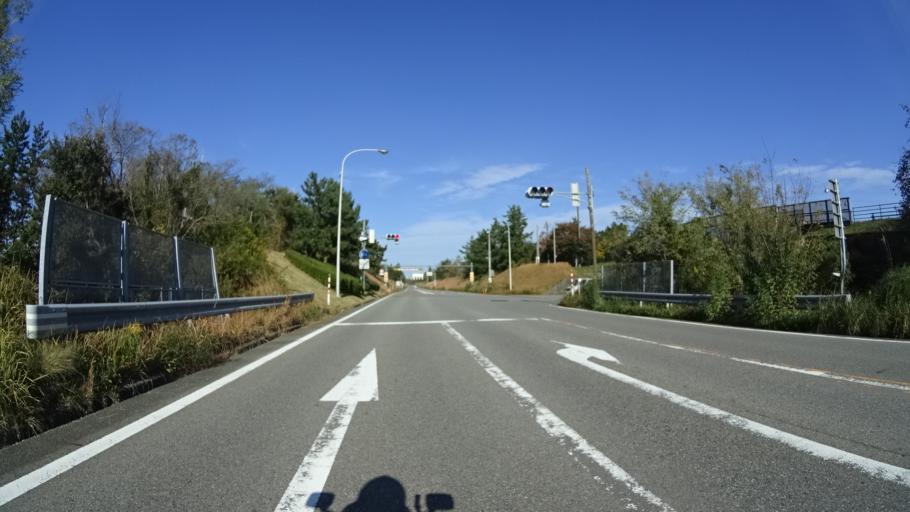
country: JP
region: Ishikawa
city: Kanazawa-shi
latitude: 36.6400
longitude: 136.6318
